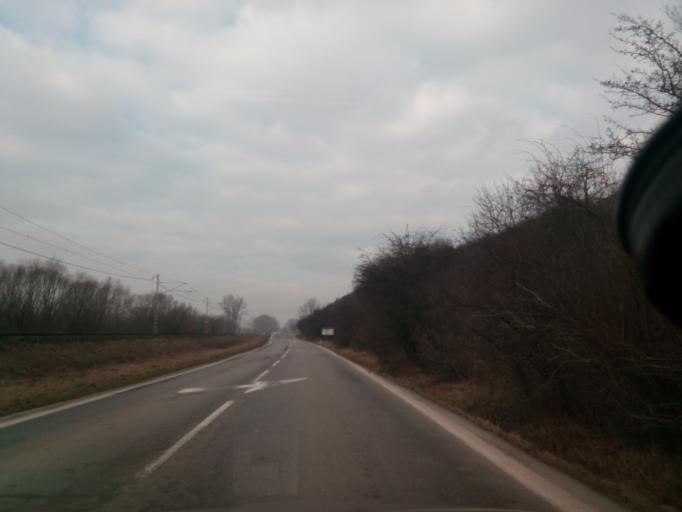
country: SK
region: Presovsky
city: Lipany
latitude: 49.1462
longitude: 20.9826
